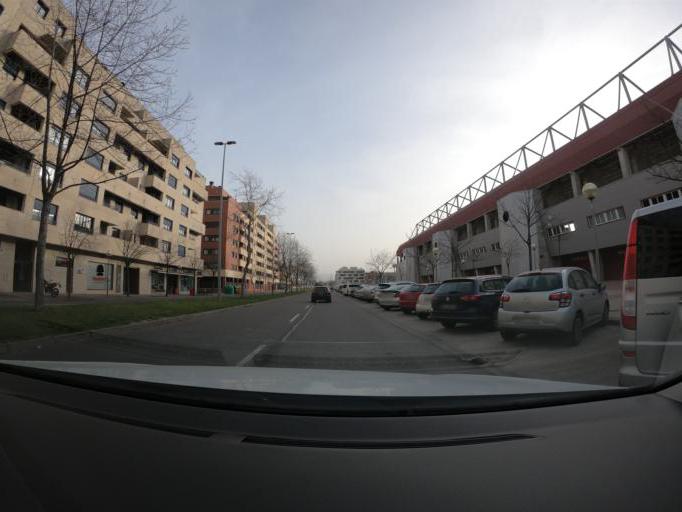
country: ES
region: La Rioja
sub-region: Provincia de La Rioja
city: Logrono
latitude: 42.4535
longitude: -2.4521
